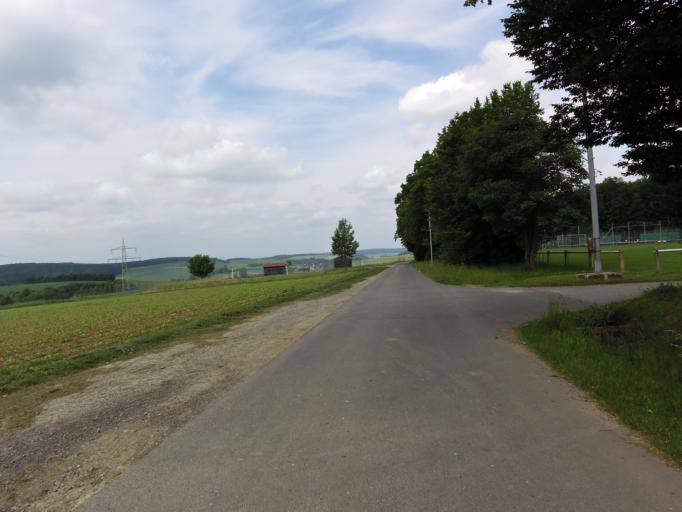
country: DE
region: Bavaria
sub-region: Regierungsbezirk Unterfranken
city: Waldbrunn
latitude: 49.7672
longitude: 9.7941
